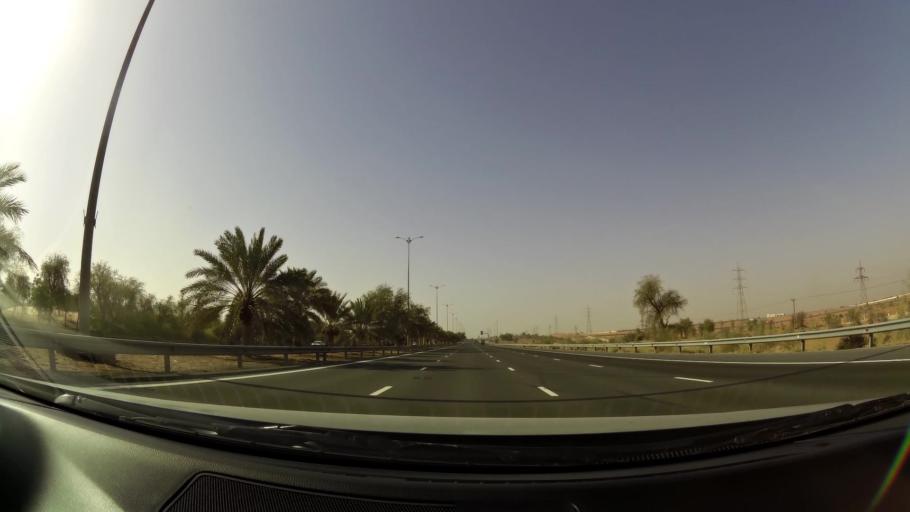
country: OM
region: Al Buraimi
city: Al Buraymi
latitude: 24.4975
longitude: 55.7692
